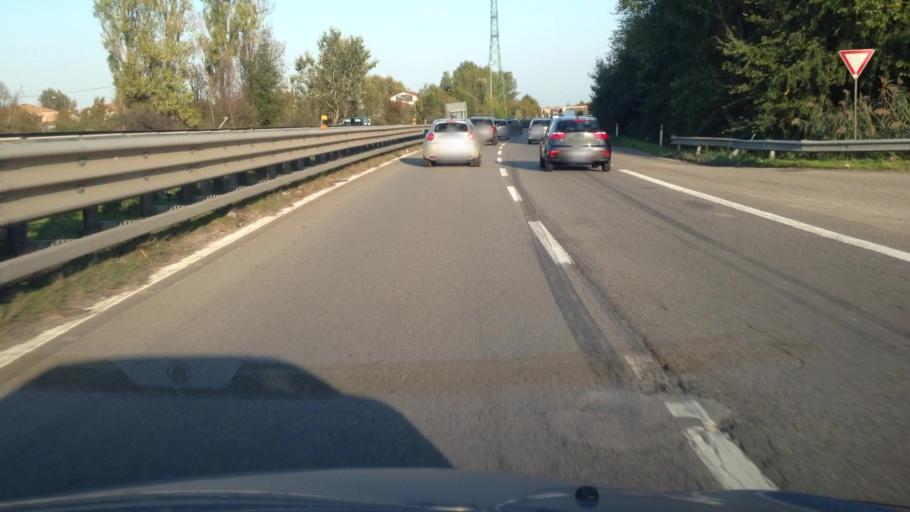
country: IT
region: Emilia-Romagna
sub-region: Provincia di Modena
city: Villanova
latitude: 44.6641
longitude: 10.8896
